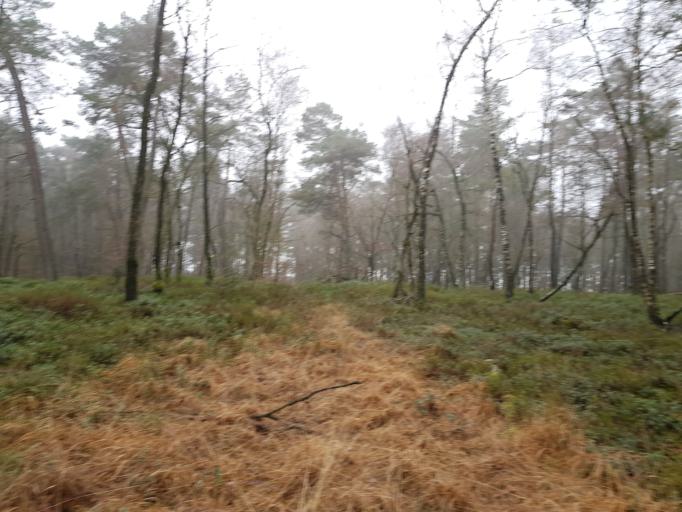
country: NL
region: Gelderland
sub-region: Gemeente Apeldoorn
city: Loenen
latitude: 52.0957
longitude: 5.9628
